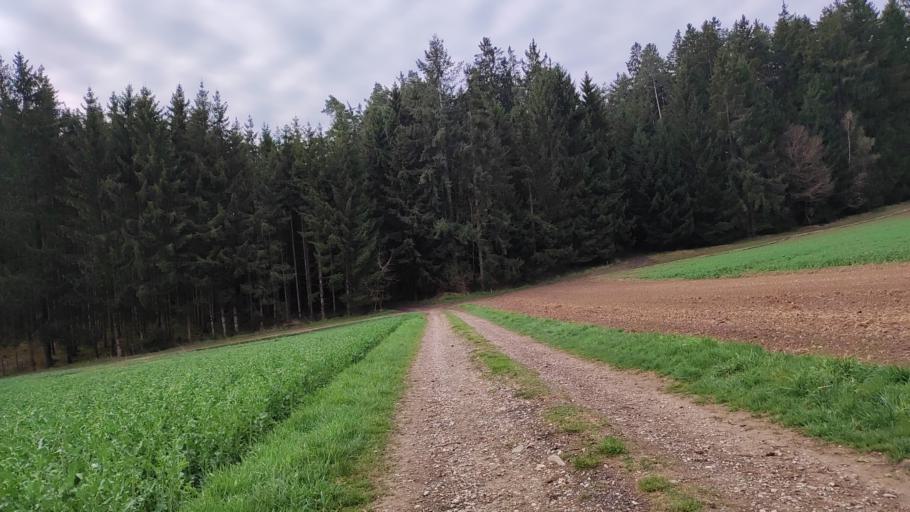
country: DE
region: Bavaria
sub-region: Swabia
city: Altenmunster
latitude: 48.4367
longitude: 10.5772
